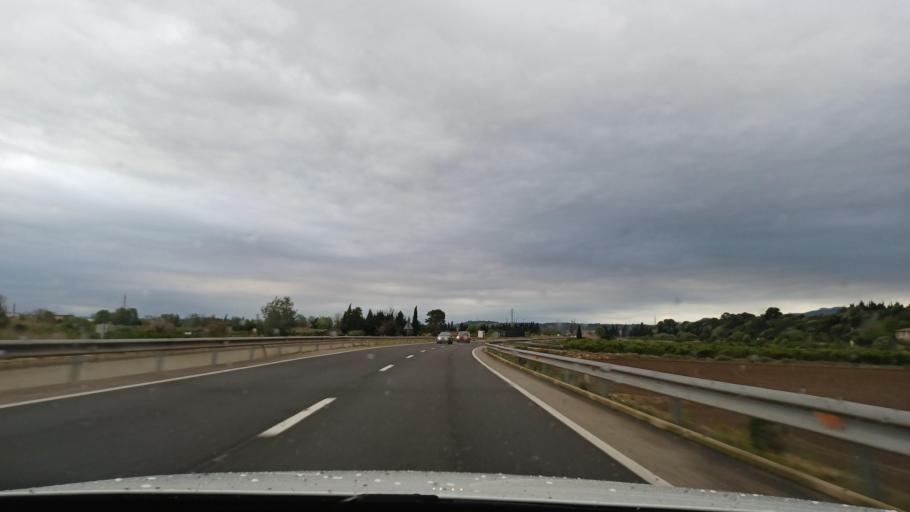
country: ES
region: Catalonia
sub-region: Provincia de Tarragona
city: Tortosa
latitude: 40.7721
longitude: 0.5287
